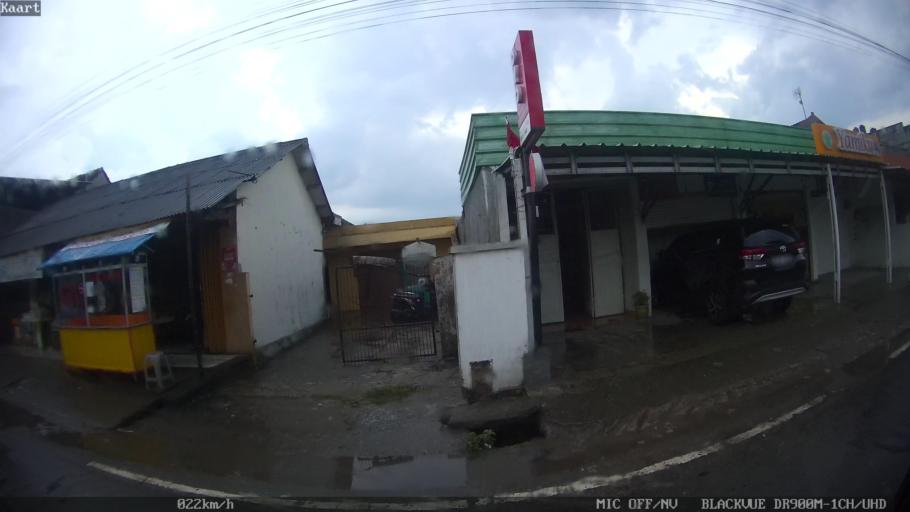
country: ID
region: Lampung
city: Kedaton
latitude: -5.3889
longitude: 105.2930
